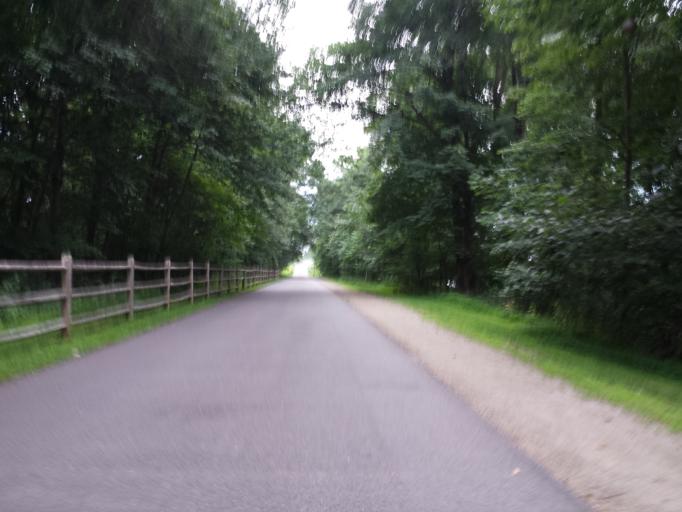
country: US
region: New York
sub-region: Dutchess County
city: Myers Corner
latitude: 41.6099
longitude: -73.8414
